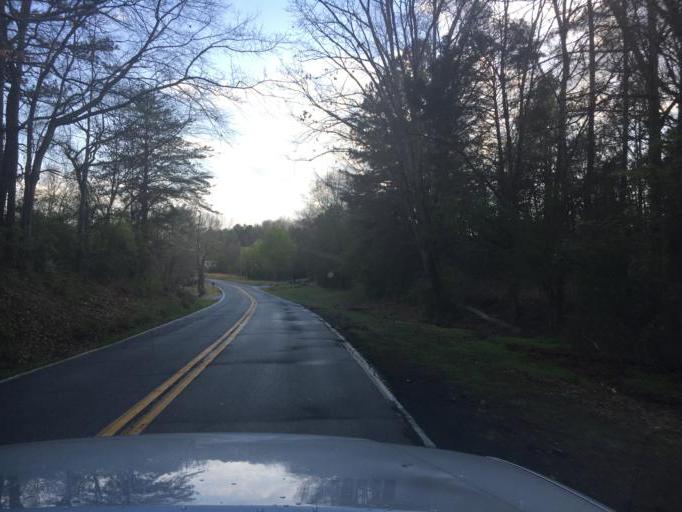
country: US
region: South Carolina
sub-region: Greenville County
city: Parker
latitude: 34.8424
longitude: -82.4944
